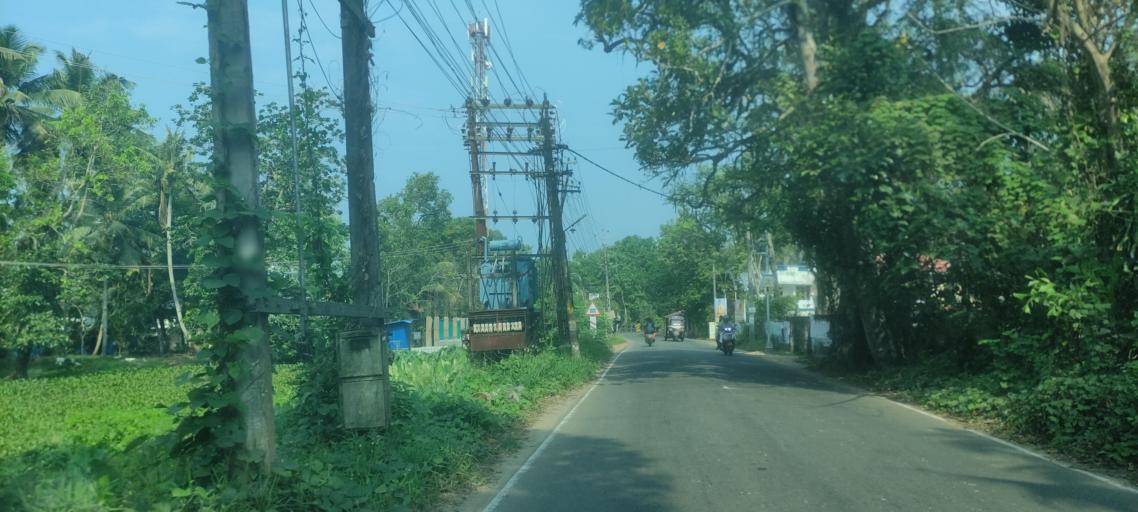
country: IN
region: Kerala
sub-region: Alappuzha
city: Kutiatodu
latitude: 9.7687
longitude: 76.3136
